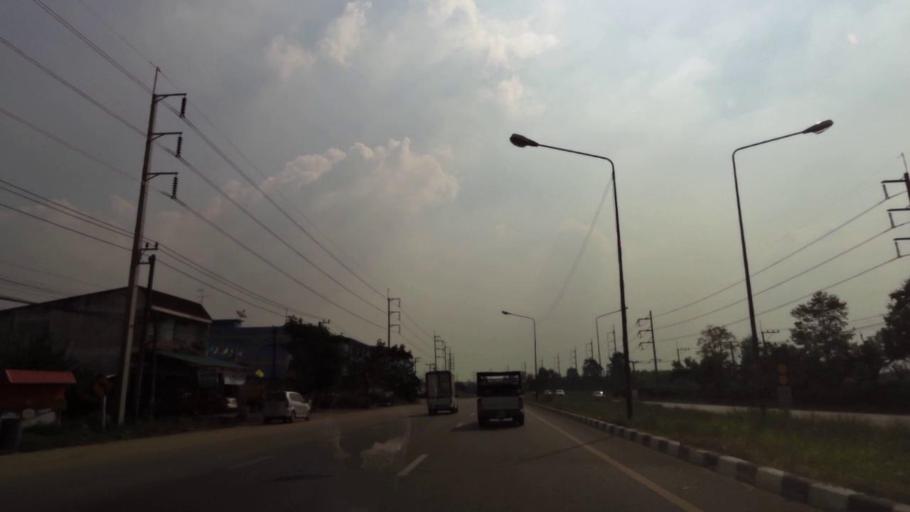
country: TH
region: Chon Buri
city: Nong Yai
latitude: 13.1995
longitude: 101.2446
